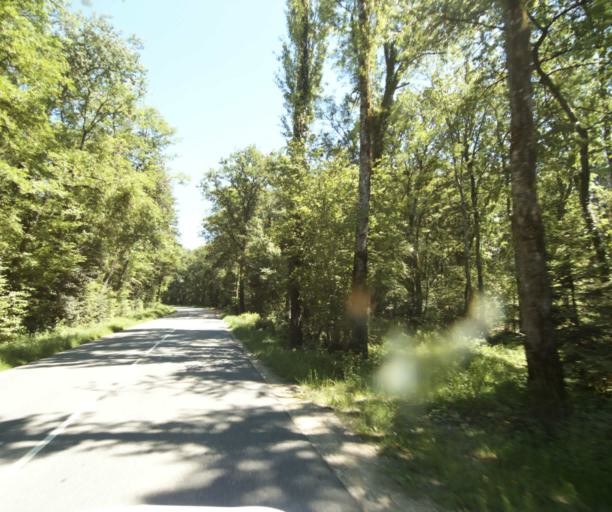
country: FR
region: Rhone-Alpes
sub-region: Departement de la Haute-Savoie
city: Loisin
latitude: 46.2680
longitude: 6.3218
